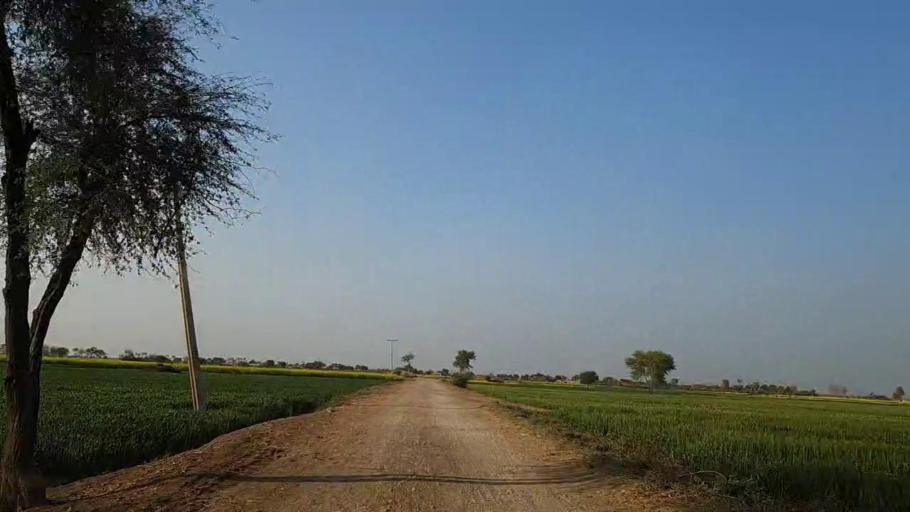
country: PK
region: Sindh
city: Sakrand
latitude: 26.1065
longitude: 68.3697
